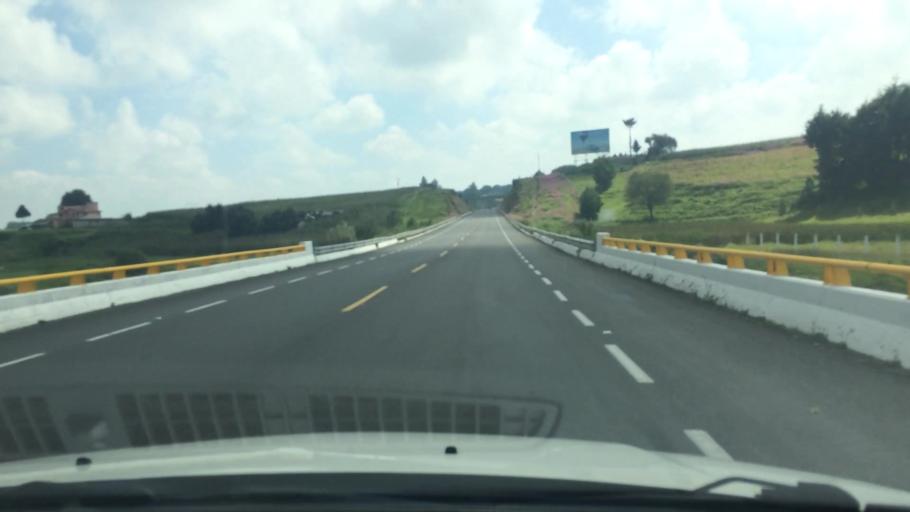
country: MX
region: Mexico
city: Amanalco de Becerra
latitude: 19.3563
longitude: -99.9654
